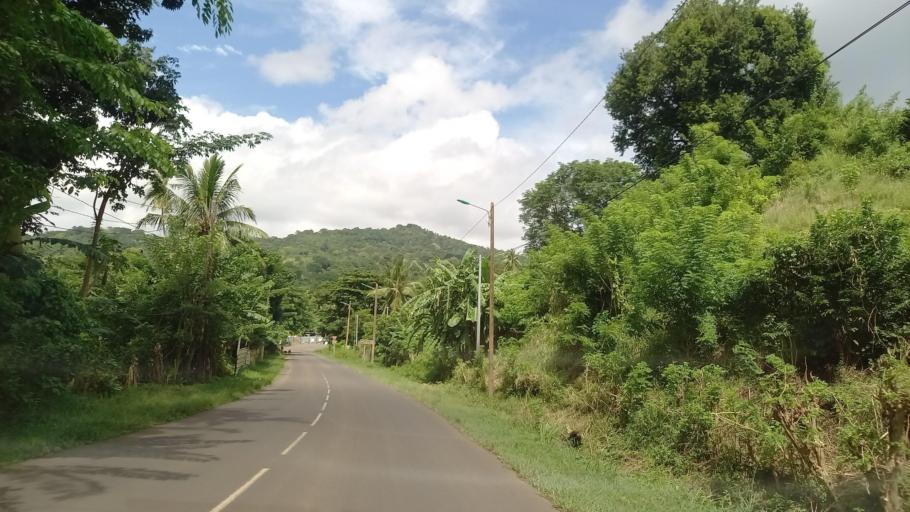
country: YT
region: Kani-Keli
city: Kani Keli
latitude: -12.9239
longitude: 45.1051
